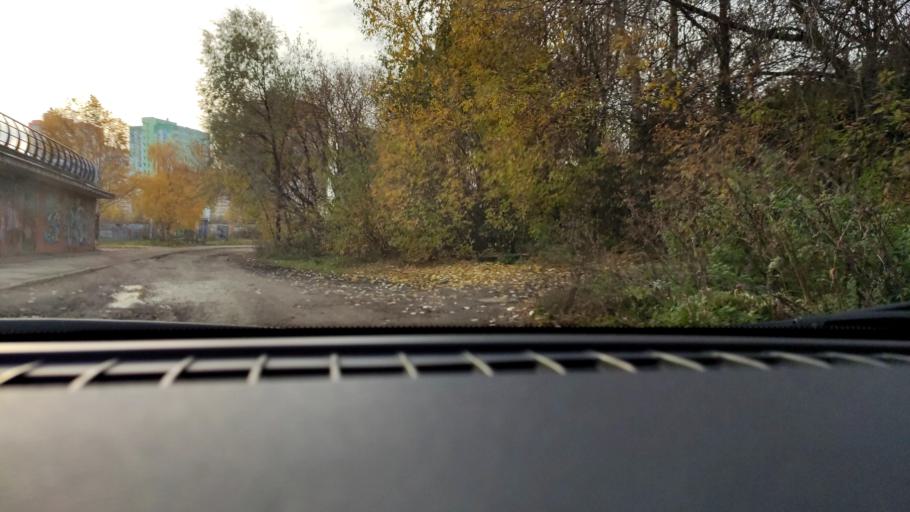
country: RU
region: Perm
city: Perm
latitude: 58.0017
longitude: 56.1975
